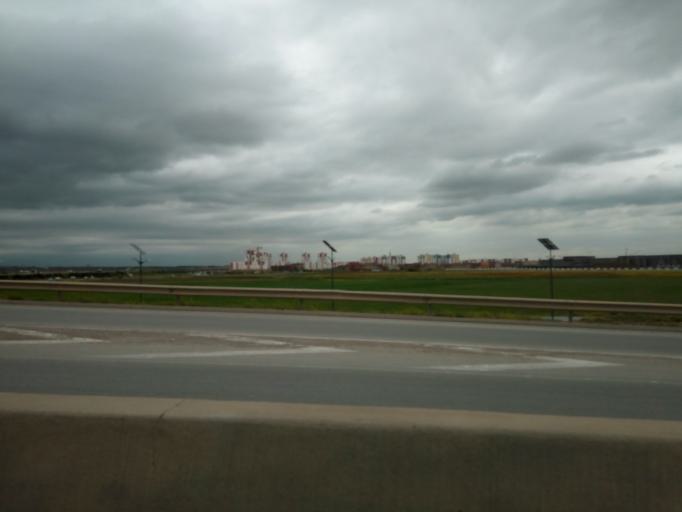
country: DZ
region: Setif
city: El Eulma
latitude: 36.1752
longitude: 5.6742
